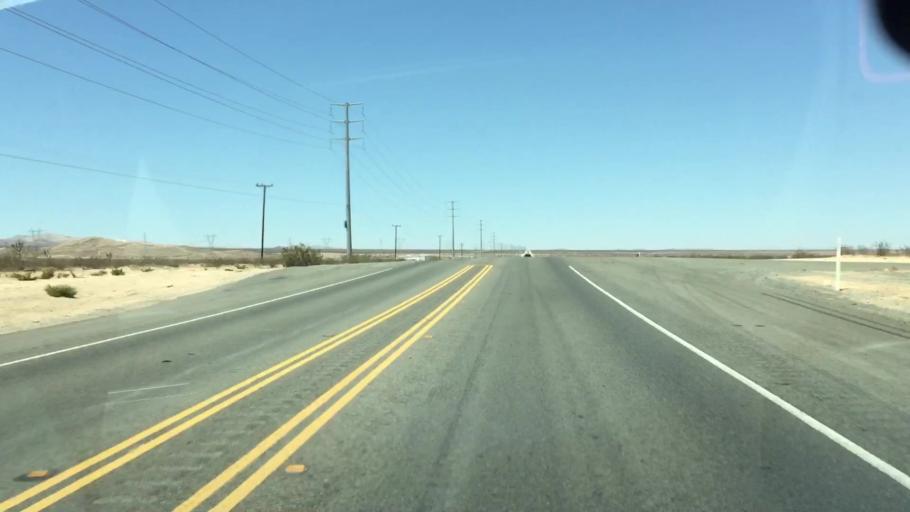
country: US
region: California
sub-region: San Bernardino County
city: Adelanto
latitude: 34.6454
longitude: -117.4347
